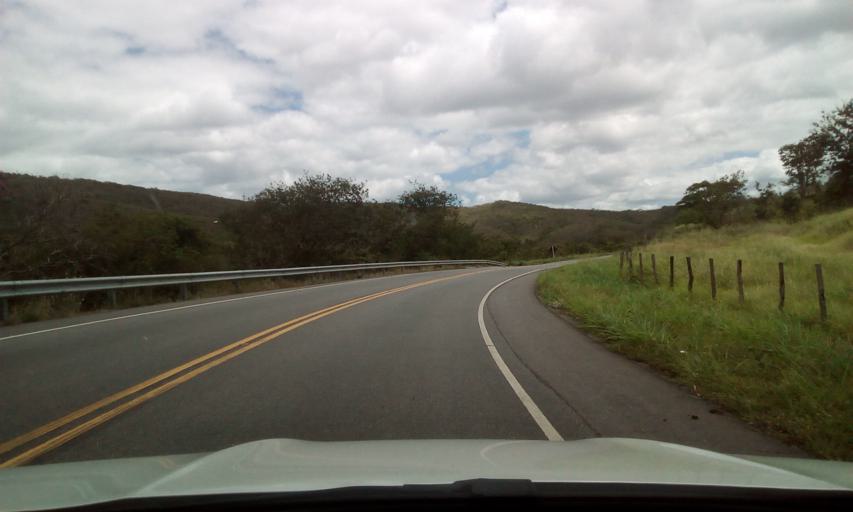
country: BR
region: Paraiba
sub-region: Serra Redonda
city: Alagoa Grande
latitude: -7.1514
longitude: -35.6128
